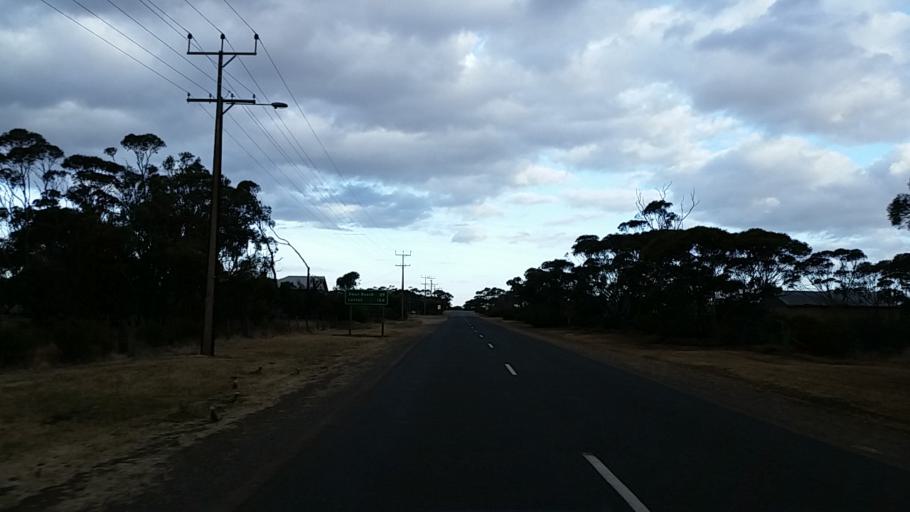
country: AU
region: South Australia
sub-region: Barossa
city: Angaston
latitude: -34.5729
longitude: 139.3005
